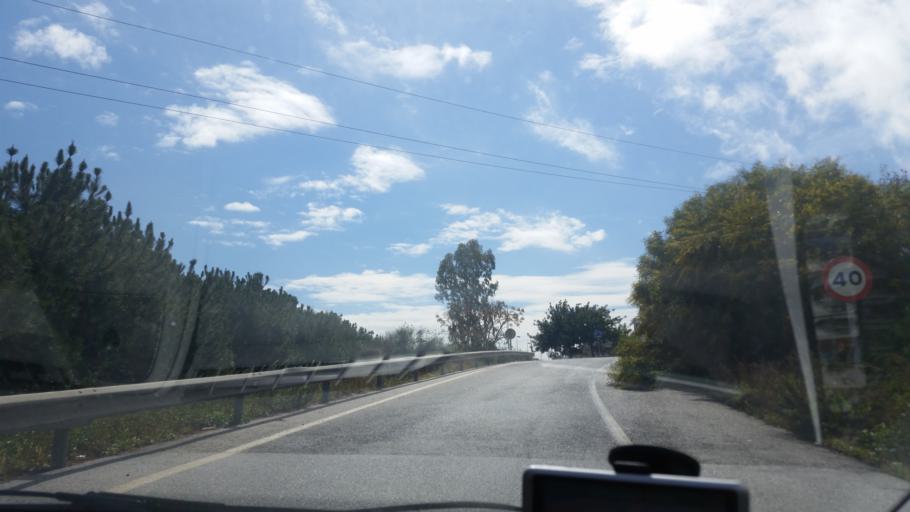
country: ES
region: Andalusia
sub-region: Provincia de Malaga
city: Fuengirola
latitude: 36.5598
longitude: -4.6208
